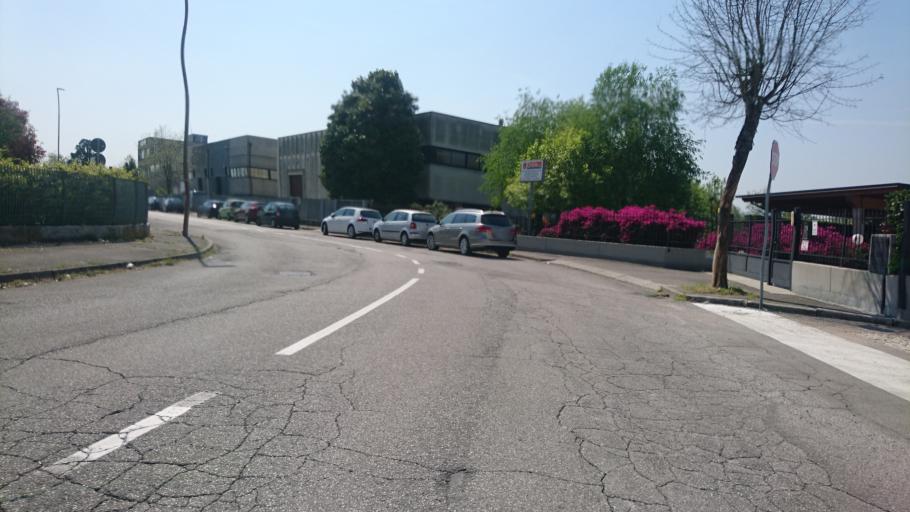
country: IT
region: Veneto
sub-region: Provincia di Padova
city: Rubano
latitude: 45.4228
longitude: 11.7882
